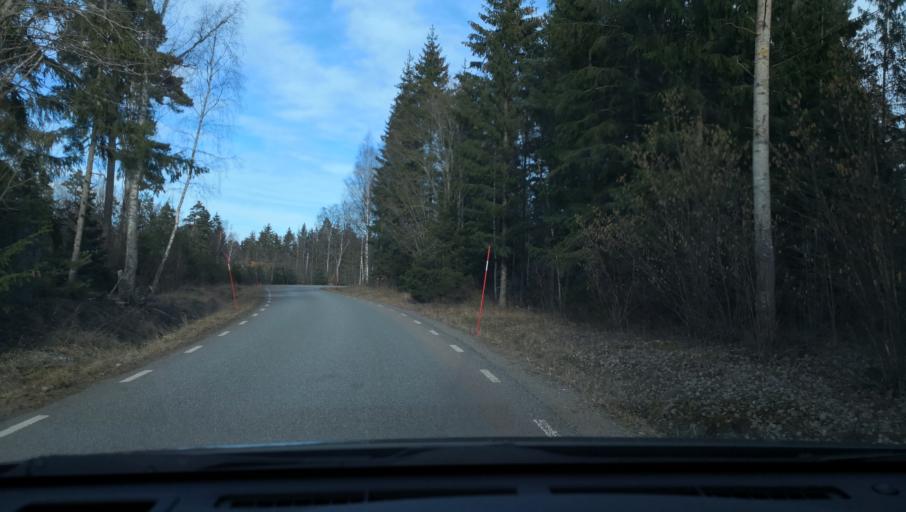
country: SE
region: Uppsala
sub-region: Enkopings Kommun
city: Grillby
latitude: 59.5400
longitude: 17.1710
